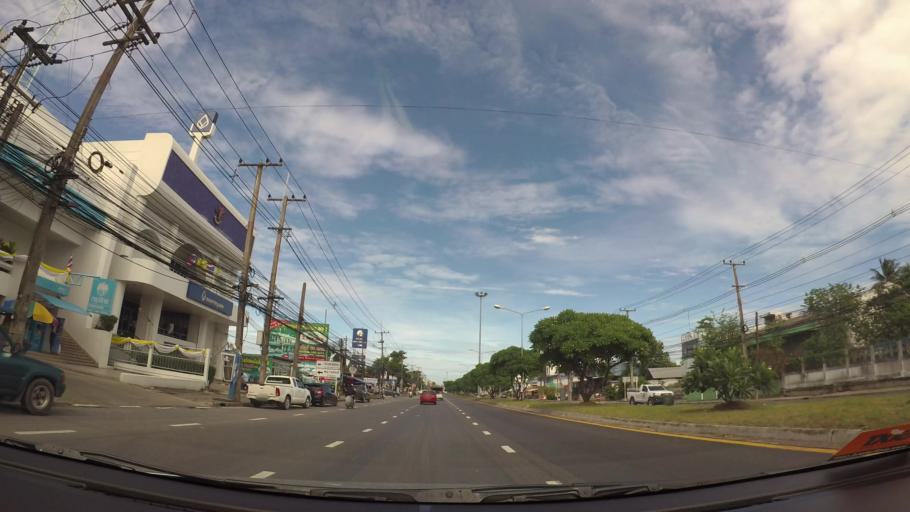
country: TH
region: Rayong
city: Ban Chang
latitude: 12.7289
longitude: 101.0636
